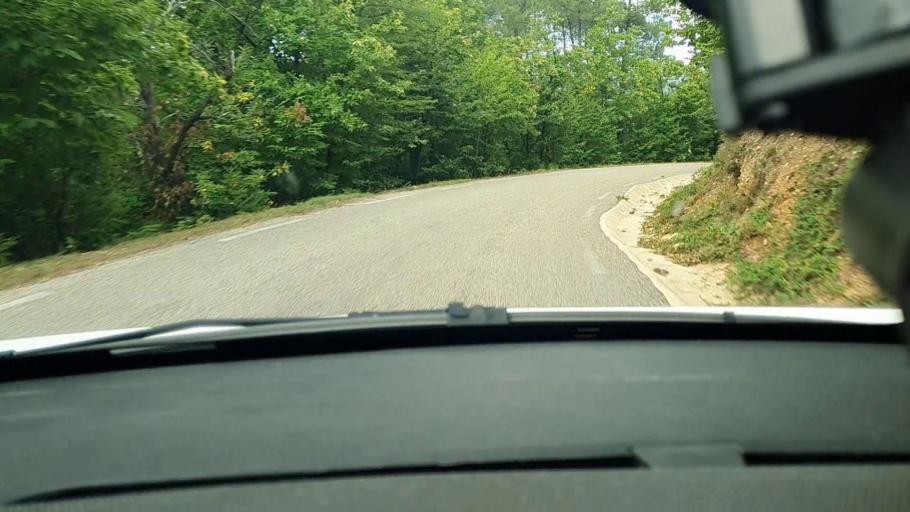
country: FR
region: Languedoc-Roussillon
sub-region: Departement du Gard
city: Branoux-les-Taillades
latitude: 44.2239
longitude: 3.9752
